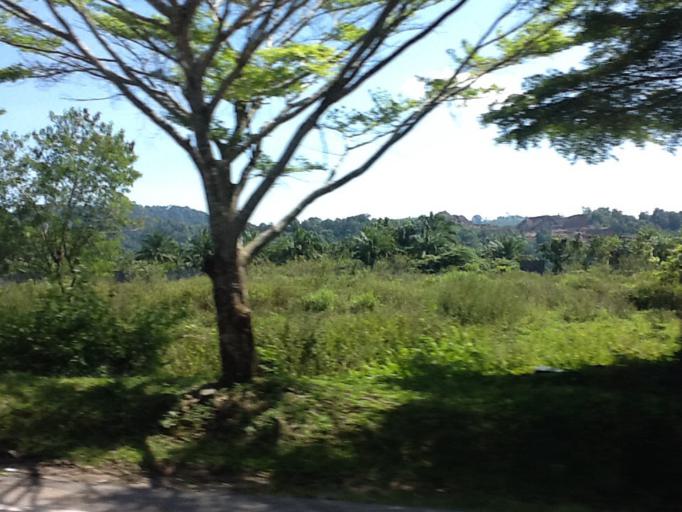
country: TH
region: Phuket
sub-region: Amphoe Kathu
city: Kathu
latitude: 7.9346
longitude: 98.3331
